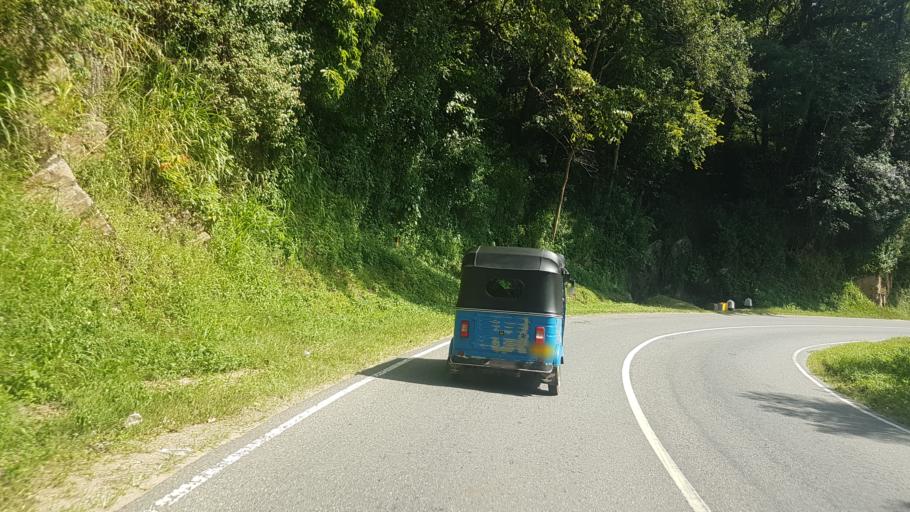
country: LK
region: Uva
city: Haputale
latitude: 6.8035
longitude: 81.0912
